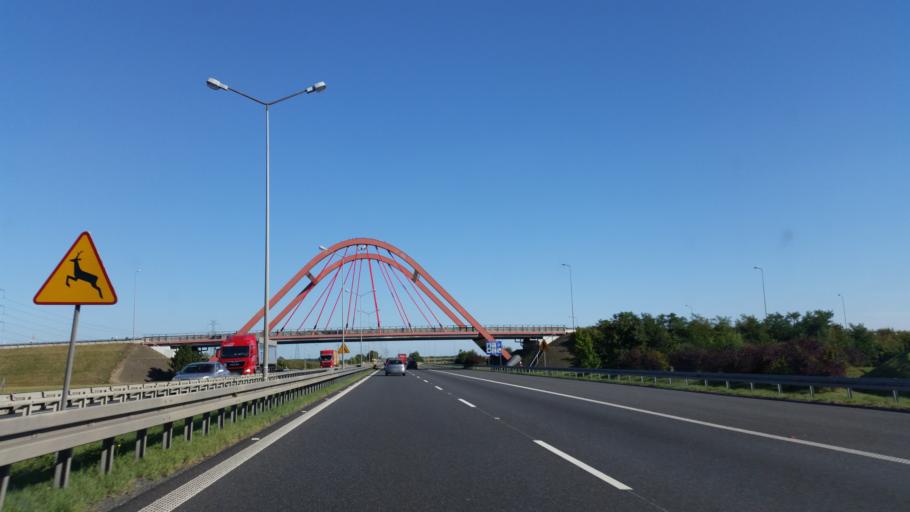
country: PL
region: Lower Silesian Voivodeship
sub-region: Powiat olawski
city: Wierzbno
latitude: 50.8794
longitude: 17.2017
